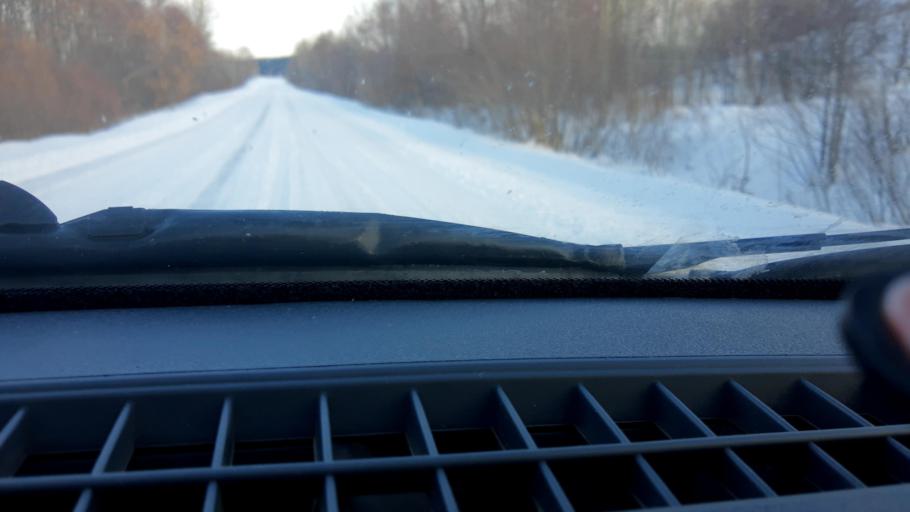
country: RU
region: Bashkortostan
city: Kushnarenkovo
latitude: 55.1391
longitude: 55.6268
